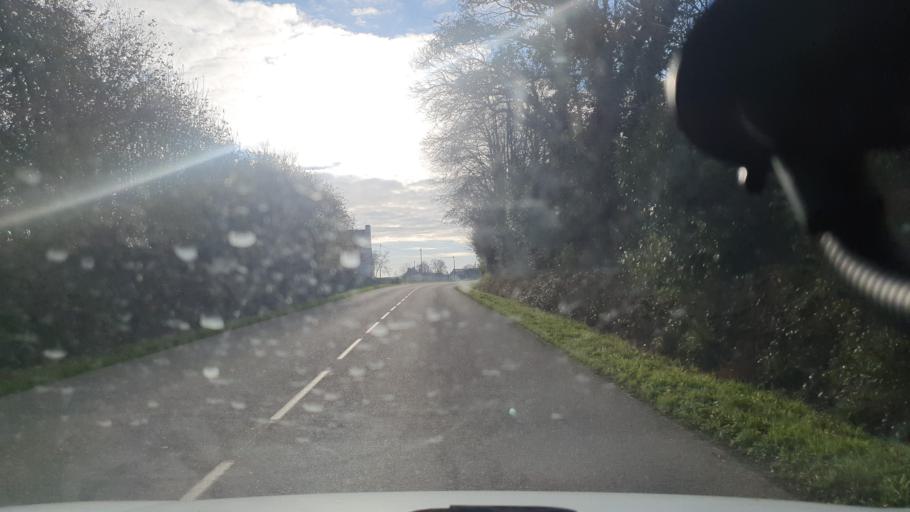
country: FR
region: Brittany
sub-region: Departement du Finistere
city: Briec
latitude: 48.0848
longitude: -4.0070
